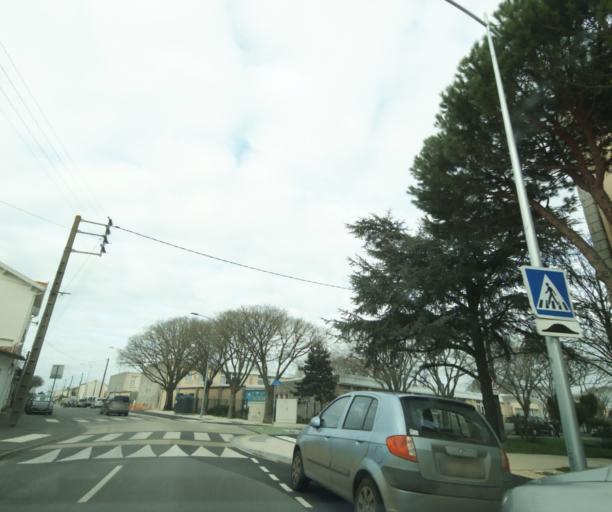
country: FR
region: Poitou-Charentes
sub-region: Departement de la Charente-Maritime
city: La Rochelle
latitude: 46.1694
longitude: -1.1637
